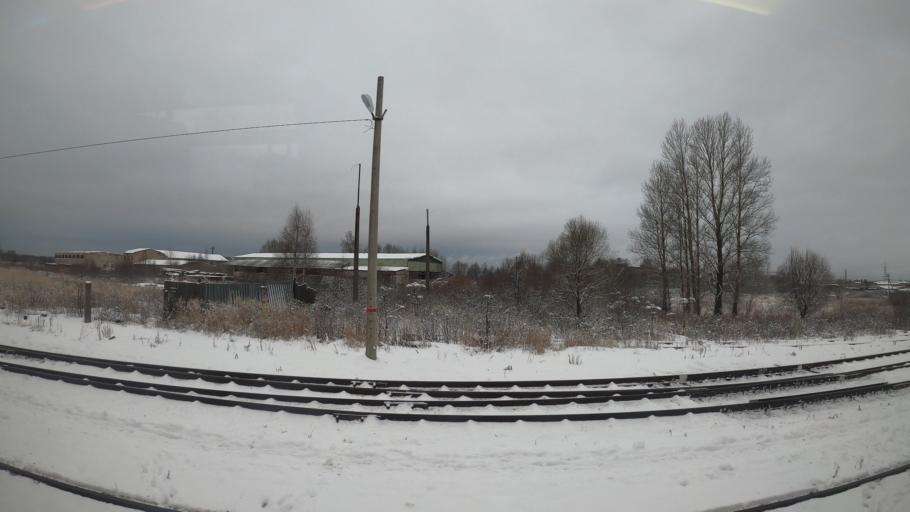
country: RU
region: Jaroslavl
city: Pereslavl'-Zalesskiy
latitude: 56.7343
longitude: 38.8929
